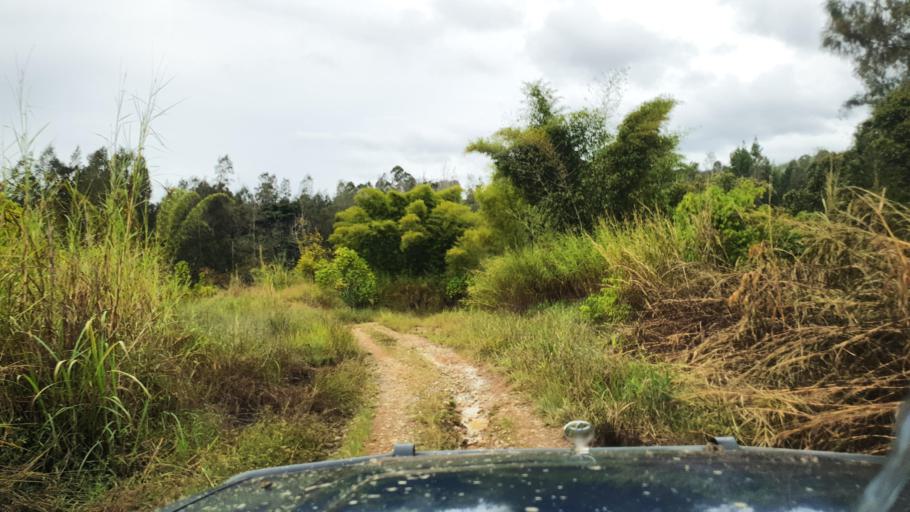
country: PG
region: Jiwaka
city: Minj
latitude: -5.9301
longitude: 144.7489
